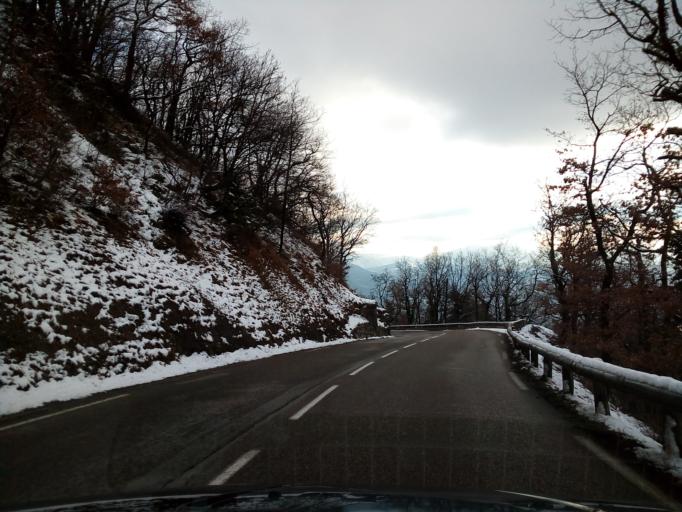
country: FR
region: Rhone-Alpes
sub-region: Departement de l'Isere
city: Corenc
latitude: 45.2271
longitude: 5.7588
